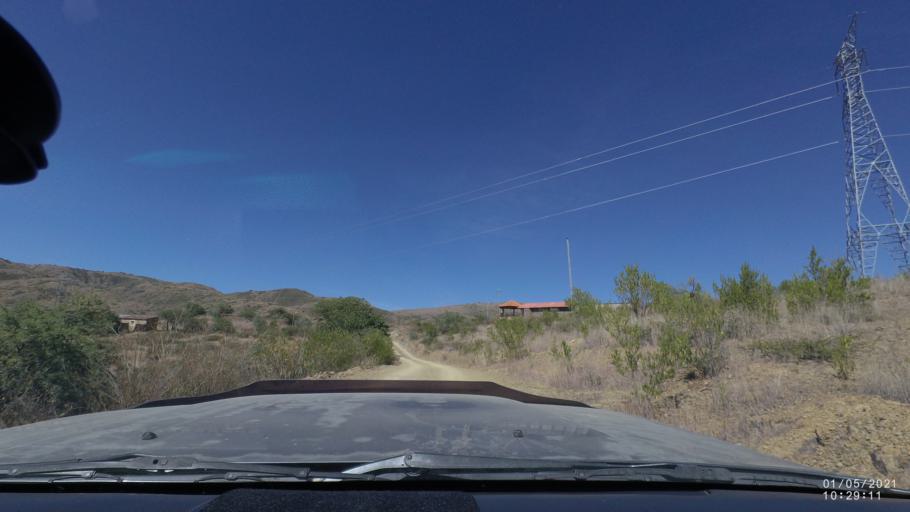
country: BO
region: Cochabamba
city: Capinota
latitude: -17.5922
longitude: -66.1901
